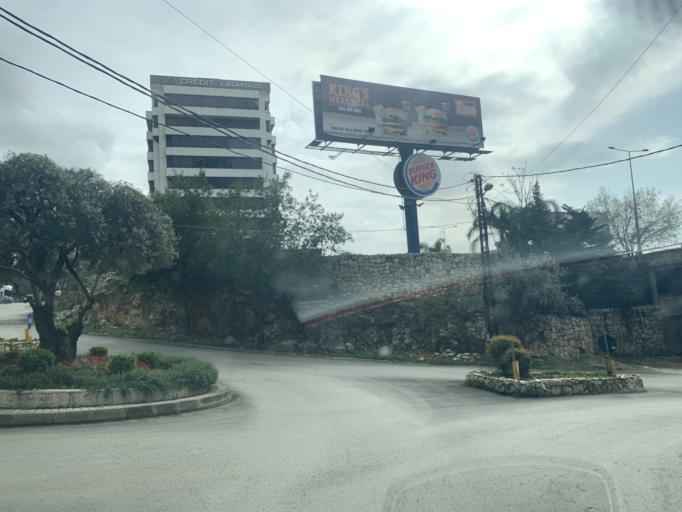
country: LB
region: Mont-Liban
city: Djounie
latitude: 33.9939
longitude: 35.6449
